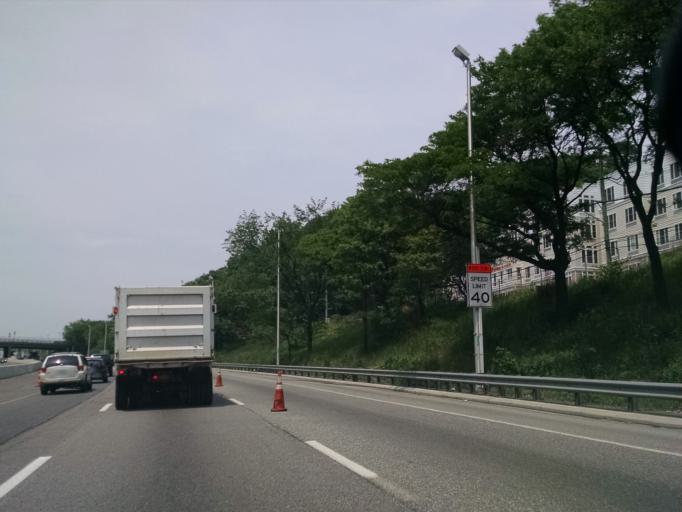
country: US
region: New Jersey
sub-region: Hudson County
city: Bayonne
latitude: 40.6106
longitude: -74.0944
